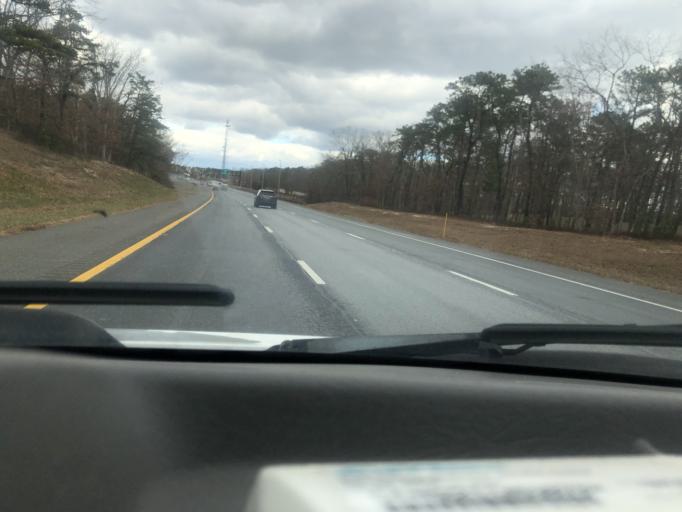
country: US
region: New Jersey
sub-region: Ocean County
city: Barnegat
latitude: 39.7521
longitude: -74.2523
